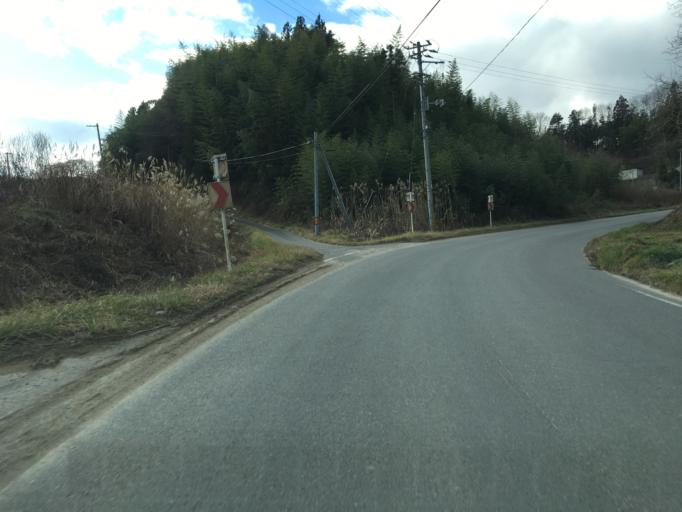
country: JP
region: Fukushima
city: Ishikawa
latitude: 37.2169
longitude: 140.5530
